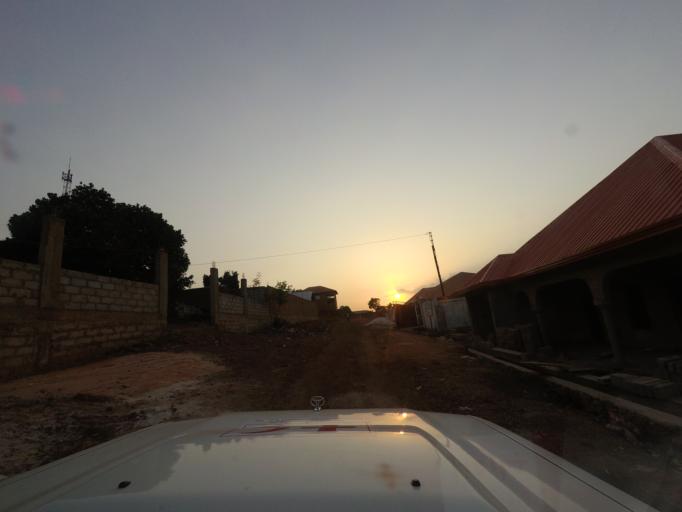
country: GN
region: Kindia
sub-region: Kindia
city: Kindia
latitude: 10.0166
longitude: -12.8891
